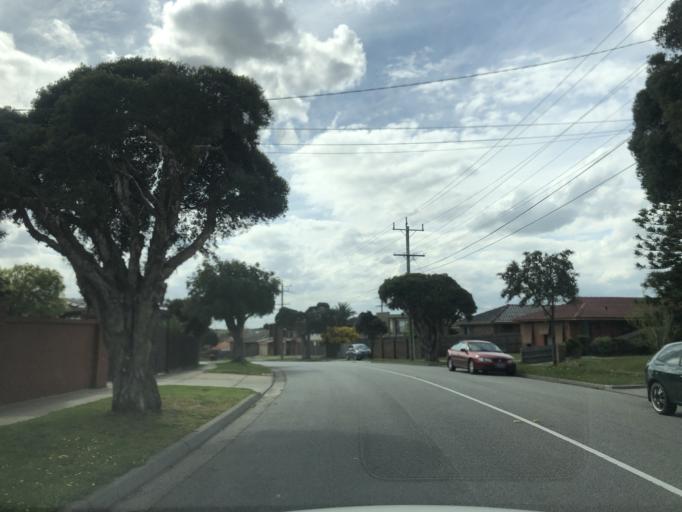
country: AU
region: Victoria
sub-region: Greater Dandenong
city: Noble Park North
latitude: -37.9519
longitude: 145.1995
